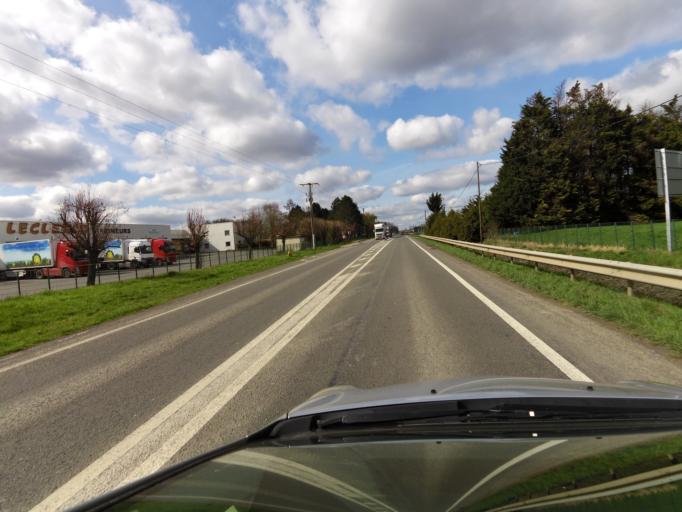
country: FR
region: Nord-Pas-de-Calais
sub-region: Departement du Pas-de-Calais
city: Violaines
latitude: 50.5547
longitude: 2.7905
